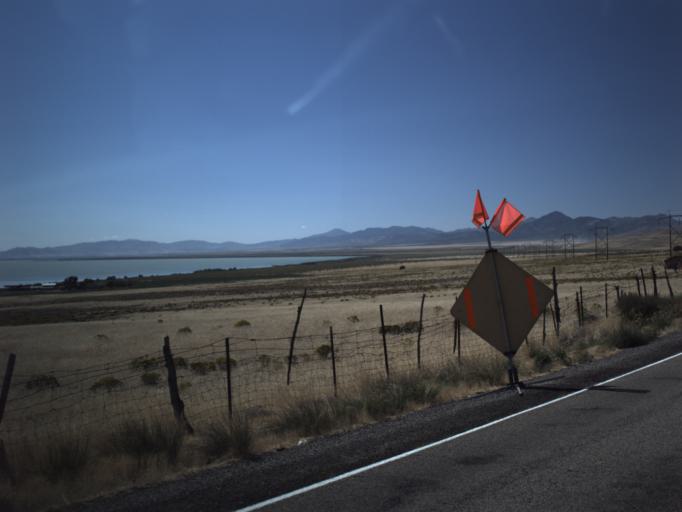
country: US
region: Utah
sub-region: Utah County
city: Eagle Mountain
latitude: 40.1814
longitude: -111.9158
